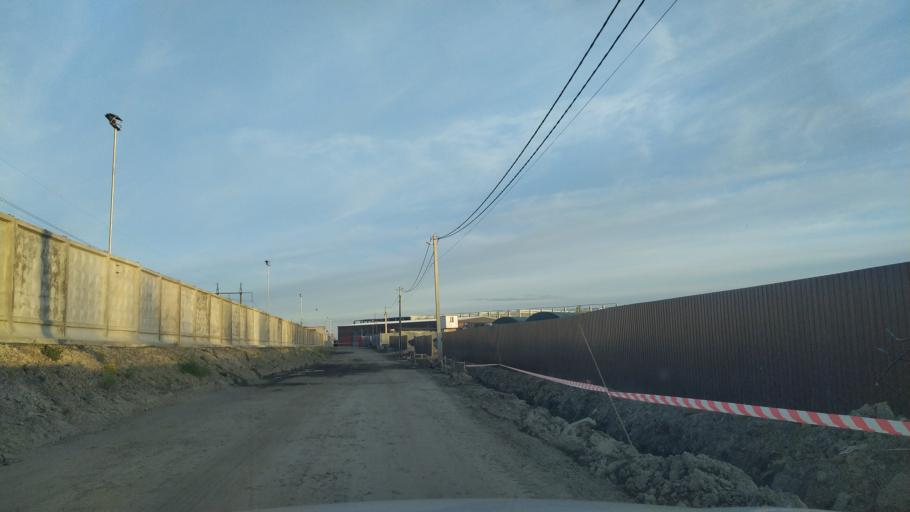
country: RU
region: St.-Petersburg
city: Obukhovo
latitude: 59.8039
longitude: 30.4599
